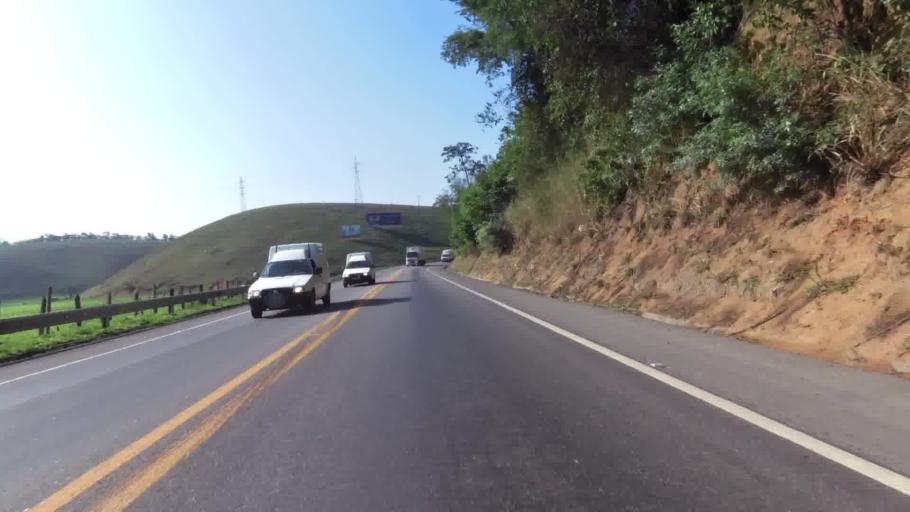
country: BR
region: Espirito Santo
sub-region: Iconha
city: Iconha
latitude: -20.7729
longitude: -40.7772
